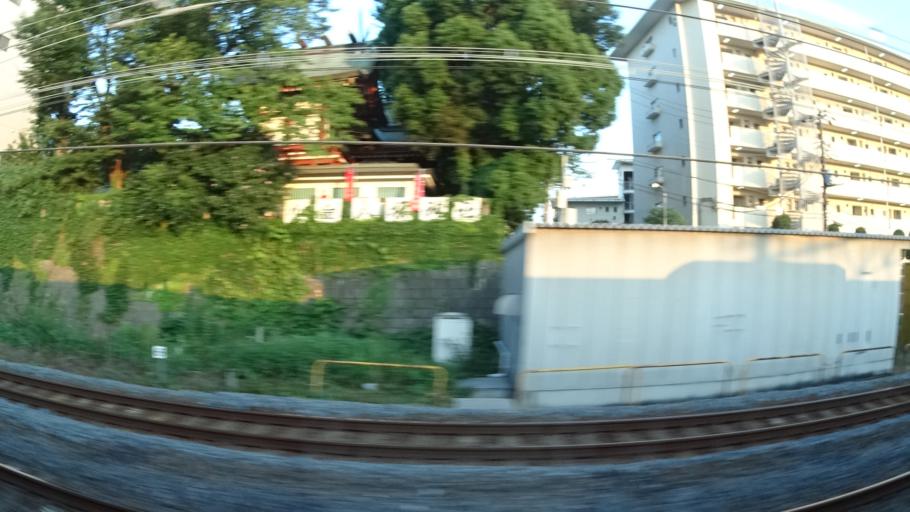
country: JP
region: Chiba
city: Nagareyama
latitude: 35.8316
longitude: 139.9274
